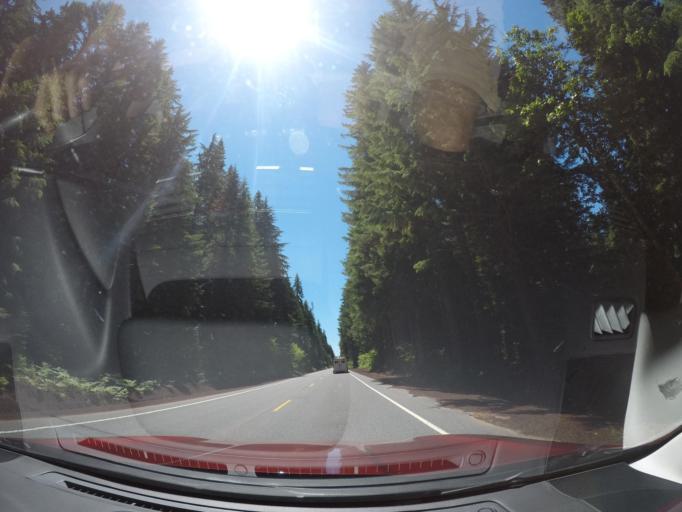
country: US
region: Oregon
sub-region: Deschutes County
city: Sisters
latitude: 44.5345
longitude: -121.9948
